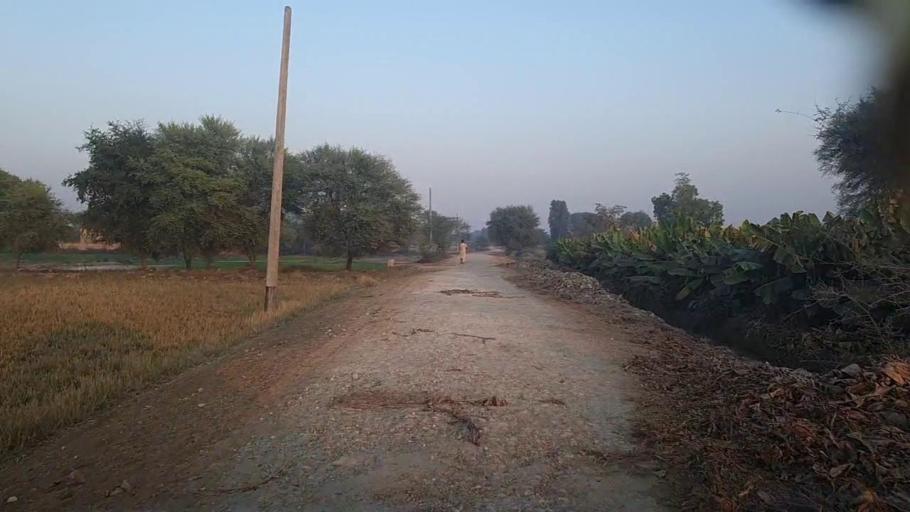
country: PK
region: Sindh
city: Karaundi
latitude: 26.8459
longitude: 68.3687
